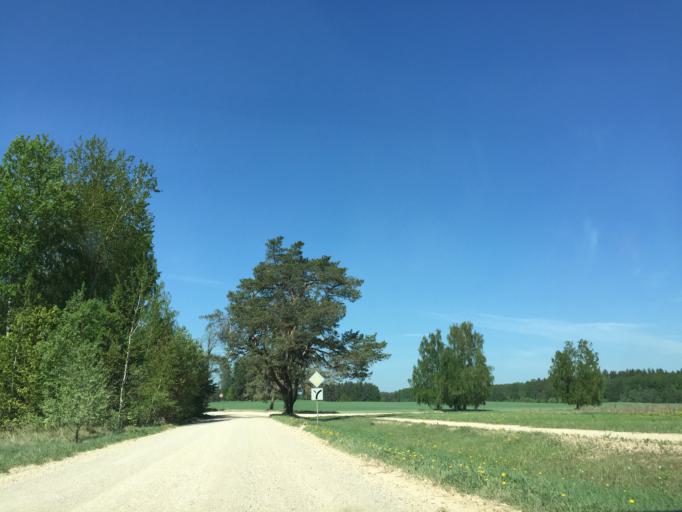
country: LV
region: Ikskile
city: Ikskile
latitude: 56.8586
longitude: 24.5016
